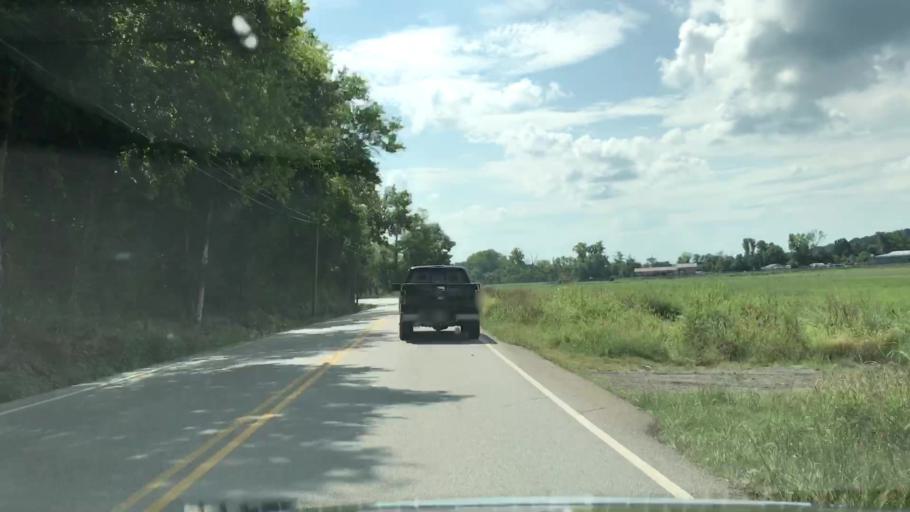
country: US
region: Tennessee
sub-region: Trousdale County
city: Hartsville
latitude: 36.4061
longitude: -86.1725
